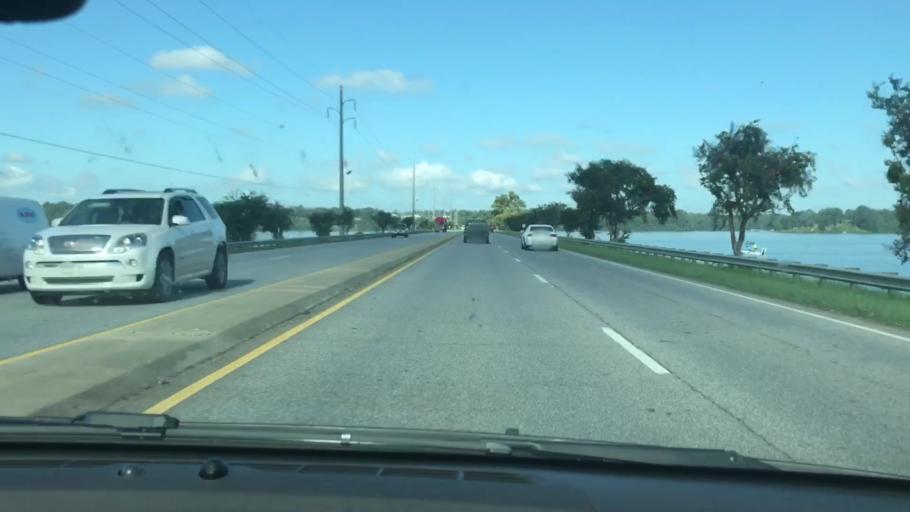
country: US
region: Georgia
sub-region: Quitman County
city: Georgetown
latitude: 31.8890
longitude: -85.1154
